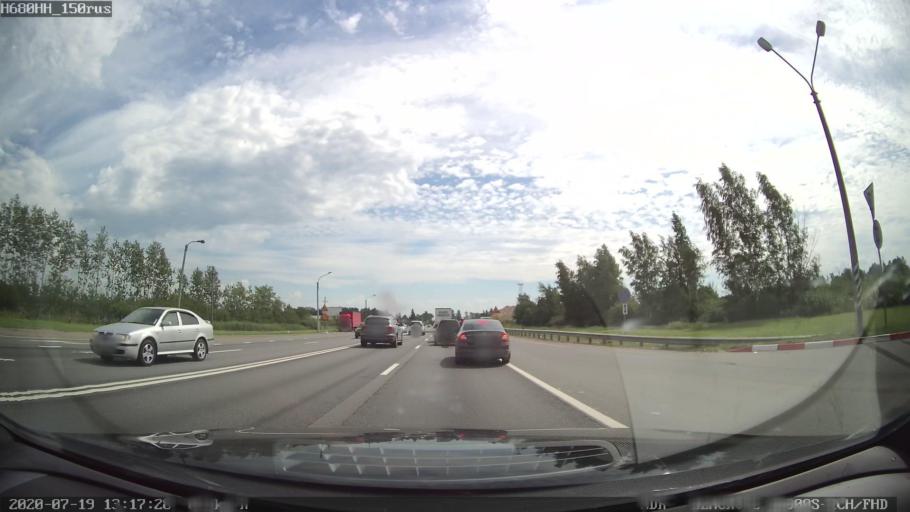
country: RU
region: St.-Petersburg
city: Kolpino
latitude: 59.7080
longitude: 30.5722
